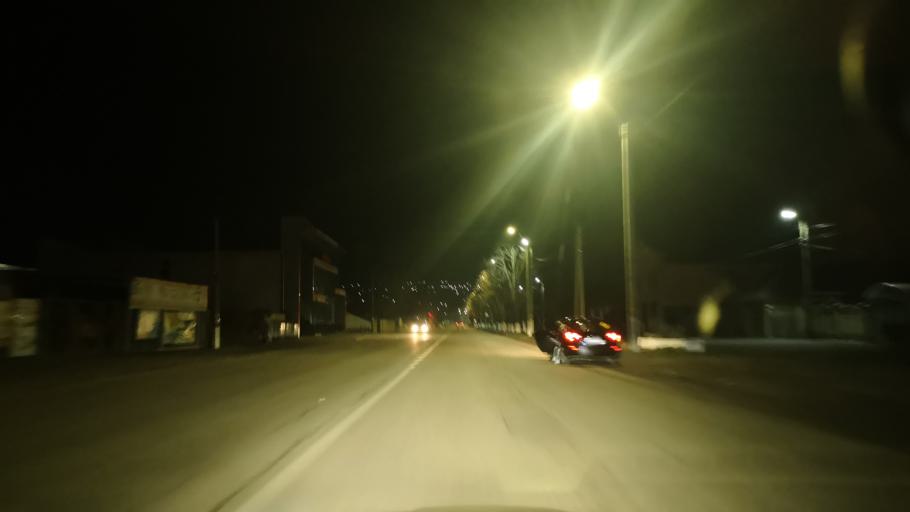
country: MD
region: Orhei
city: Orhei
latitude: 47.3615
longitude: 28.8123
